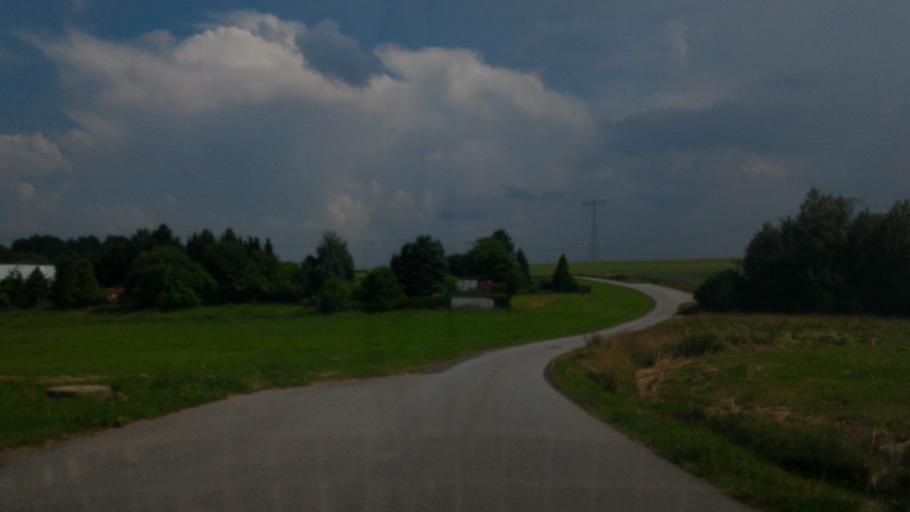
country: DE
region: Saxony
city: Hirschfelde
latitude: 50.9406
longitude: 14.8377
